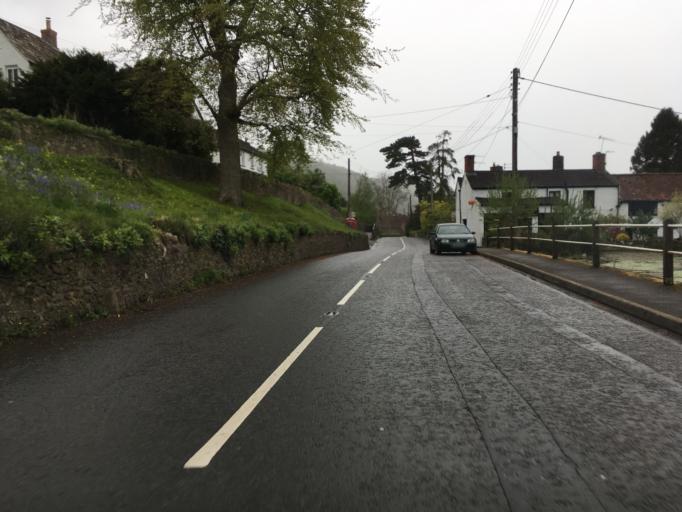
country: GB
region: England
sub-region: Bath and North East Somerset
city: Compton Martin
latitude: 51.3105
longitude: -2.6543
